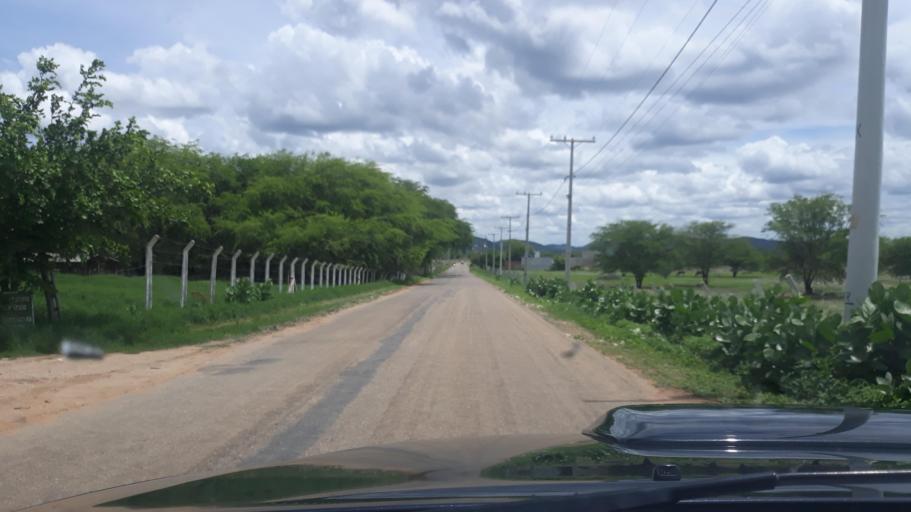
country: BR
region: Bahia
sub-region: Guanambi
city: Guanambi
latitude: -14.2961
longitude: -42.6967
